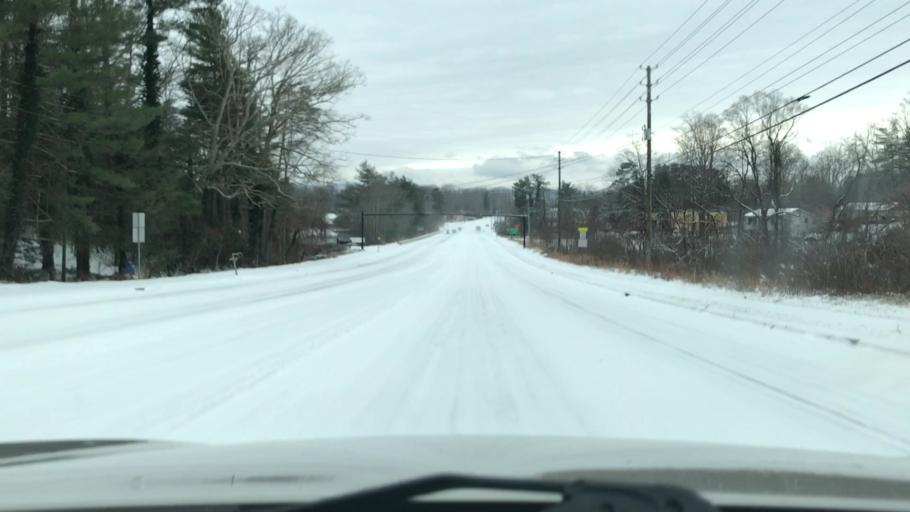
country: US
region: North Carolina
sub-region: Buncombe County
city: Royal Pines
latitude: 35.4842
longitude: -82.5300
